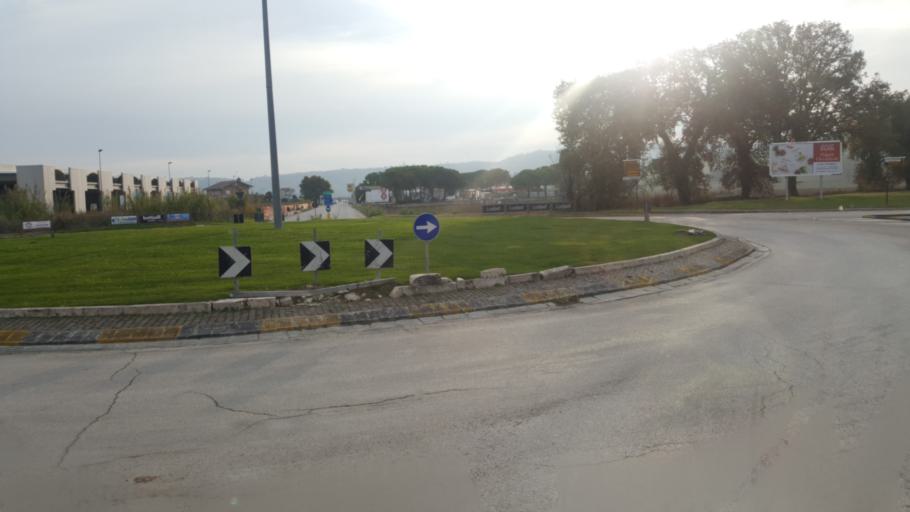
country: IT
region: The Marches
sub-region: Provincia di Macerata
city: Borgo Stazione
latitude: 43.2686
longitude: 13.6632
